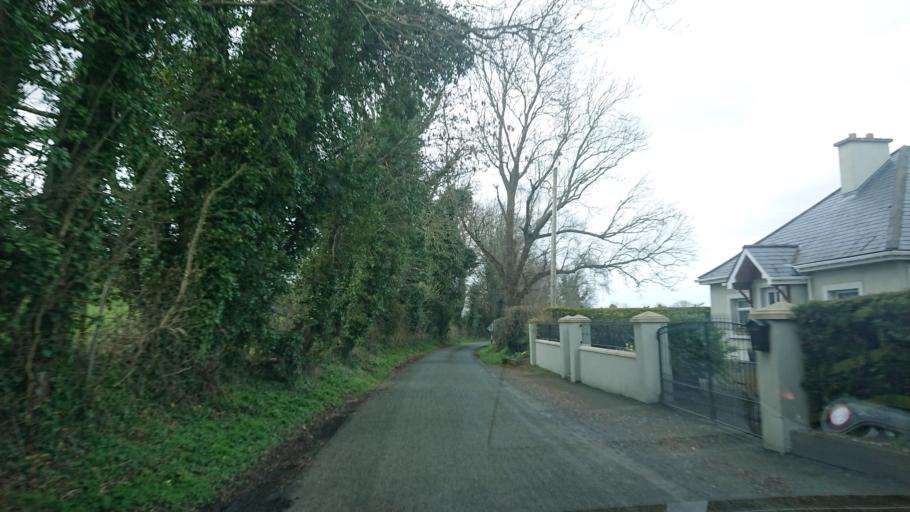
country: IE
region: Leinster
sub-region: Kildare
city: Eadestown
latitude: 53.1672
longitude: -6.6130
